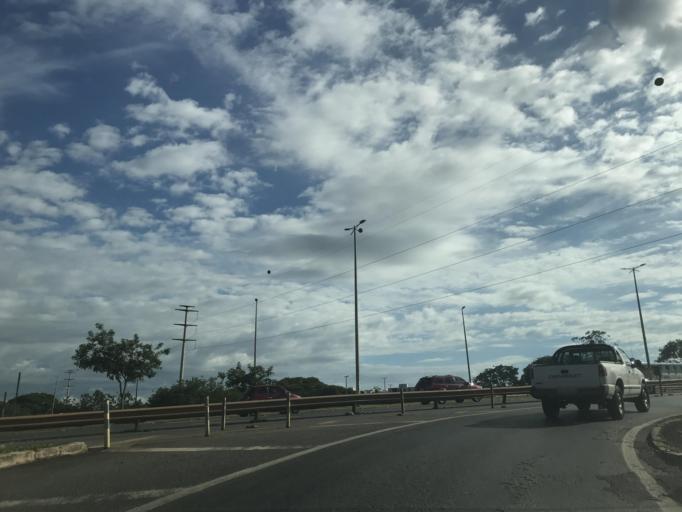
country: BR
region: Federal District
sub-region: Brasilia
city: Brasilia
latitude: -15.8115
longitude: -47.9516
